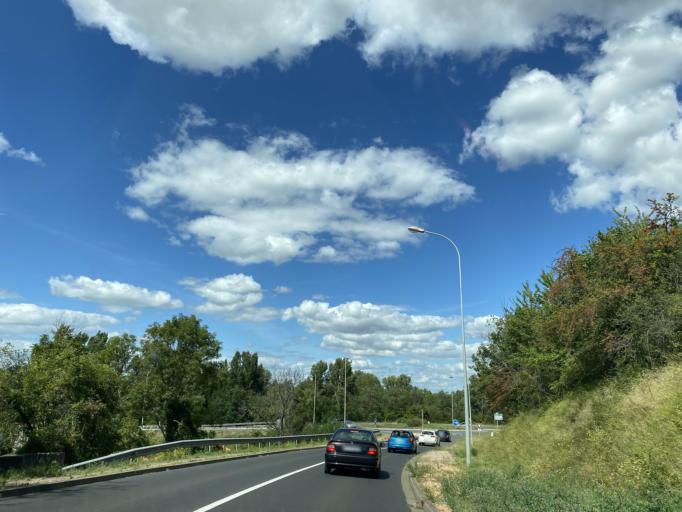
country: FR
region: Auvergne
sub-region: Departement du Puy-de-Dome
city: Dallet
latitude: 45.7732
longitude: 3.2399
